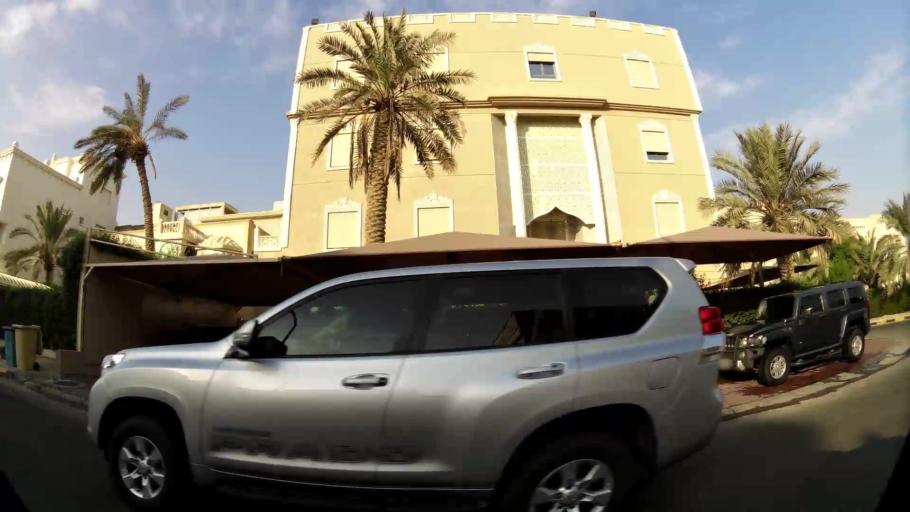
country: KW
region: Muhafazat Hawalli
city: Ar Rumaythiyah
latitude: 29.3196
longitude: 48.0728
